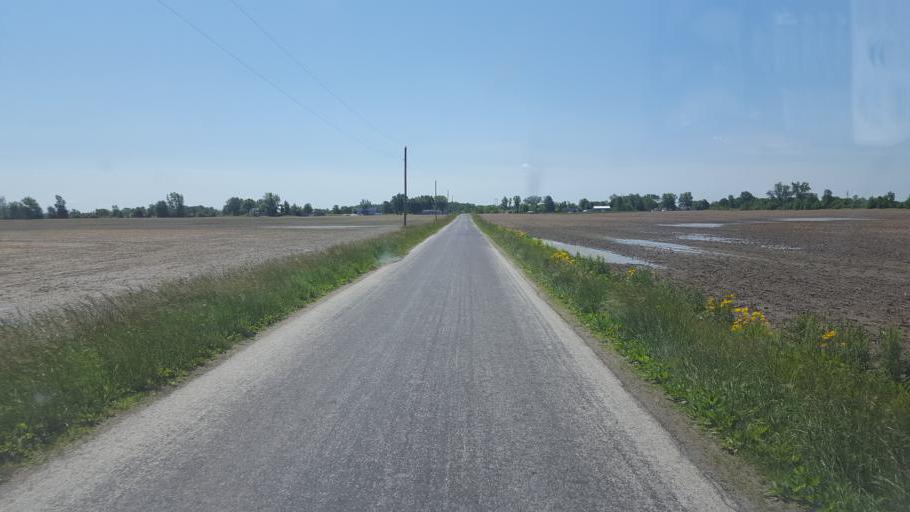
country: US
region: Ohio
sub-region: Union County
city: Richwood
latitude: 40.5774
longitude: -83.4075
